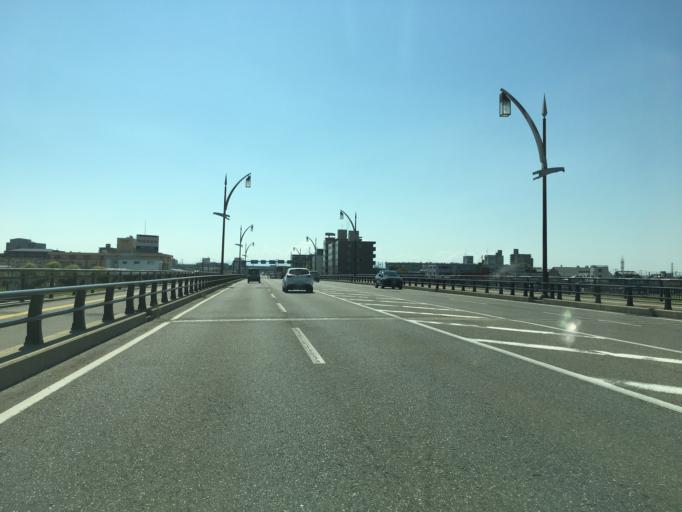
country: JP
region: Niigata
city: Niigata-shi
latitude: 37.9125
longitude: 139.0431
